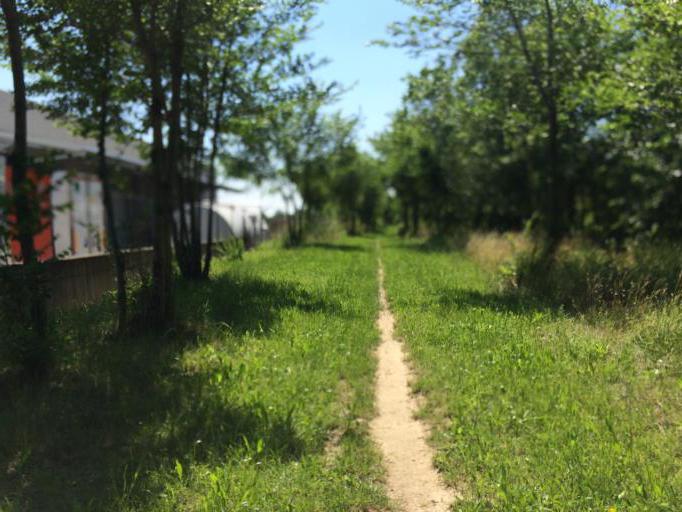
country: IT
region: Veneto
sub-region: Provincia di Vicenza
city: Sossano
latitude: 45.3519
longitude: 11.5039
